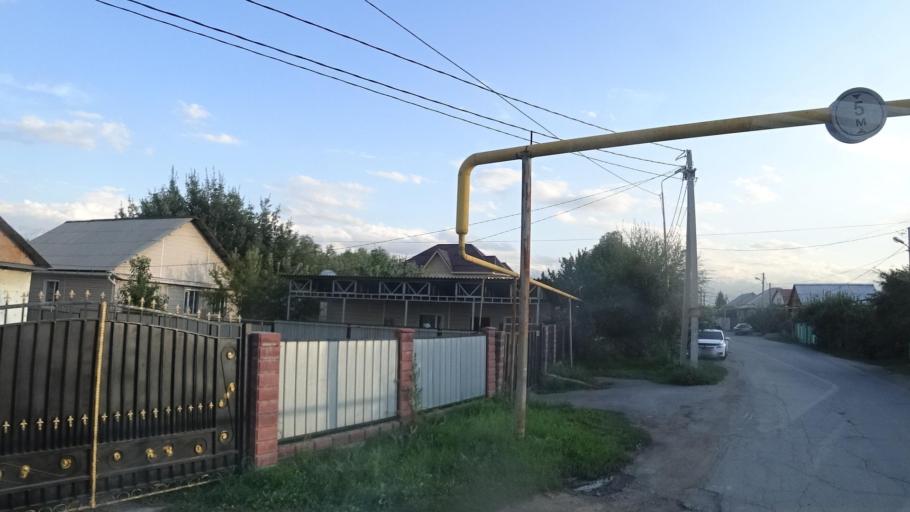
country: KZ
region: Almaty Oblysy
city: Pervomayskiy
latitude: 43.3320
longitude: 76.9929
